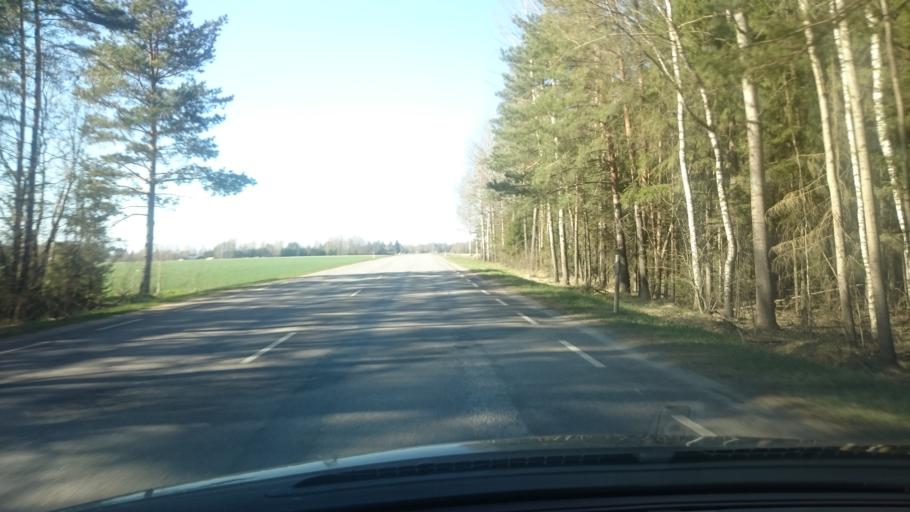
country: EE
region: Tartu
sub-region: UElenurme vald
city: Ulenurme
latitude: 58.3227
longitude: 26.9833
